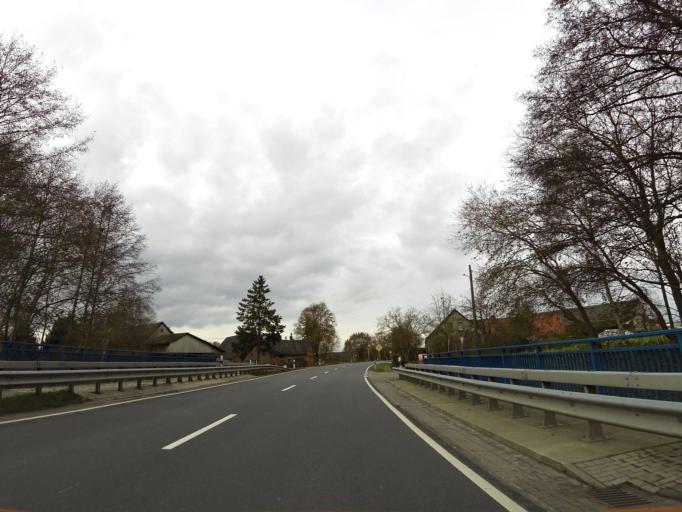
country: DE
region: Lower Saxony
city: Bergen an der Dumme
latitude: 52.9000
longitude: 10.9294
